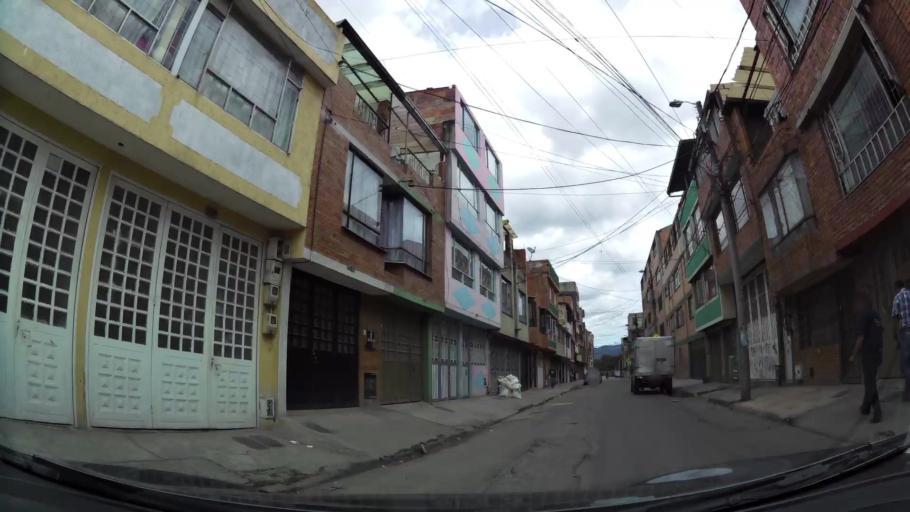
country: CO
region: Cundinamarca
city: Funza
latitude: 4.7054
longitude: -74.1308
